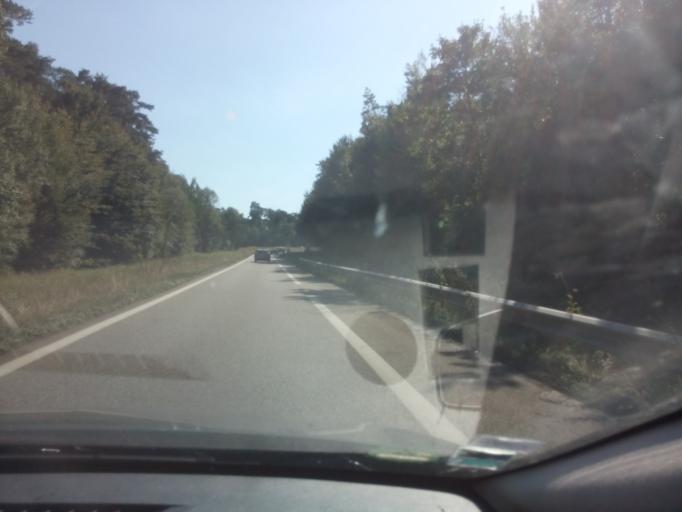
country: FR
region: Alsace
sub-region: Departement du Bas-Rhin
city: Niederschaeffolsheim
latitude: 48.7935
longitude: 7.7449
